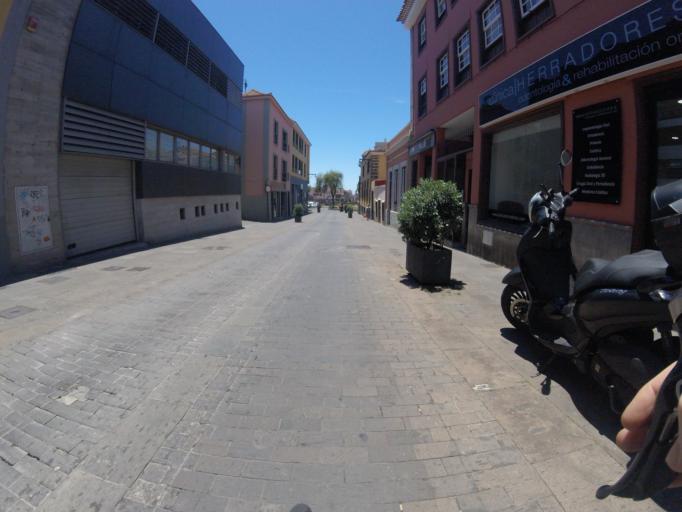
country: ES
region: Canary Islands
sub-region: Provincia de Santa Cruz de Tenerife
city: La Laguna
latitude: 28.4860
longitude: -16.3147
